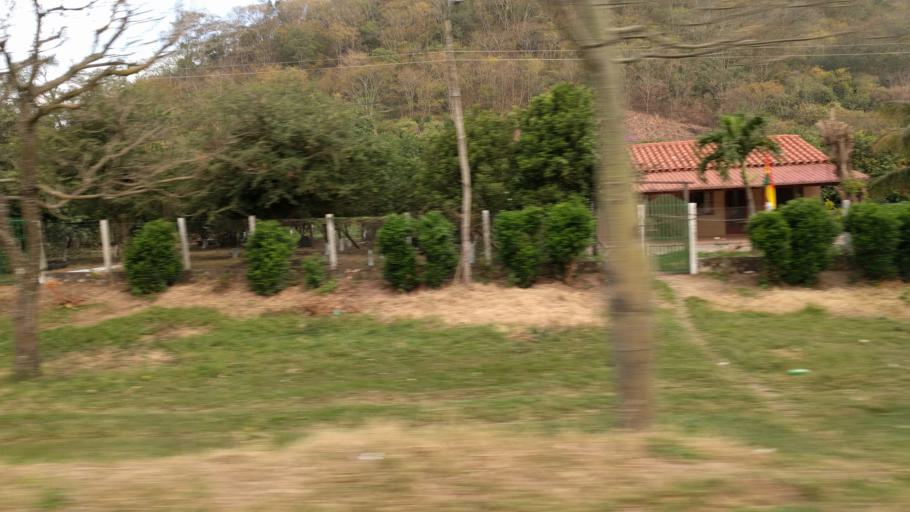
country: BO
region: Santa Cruz
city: Jorochito
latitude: -18.0708
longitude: -63.4406
